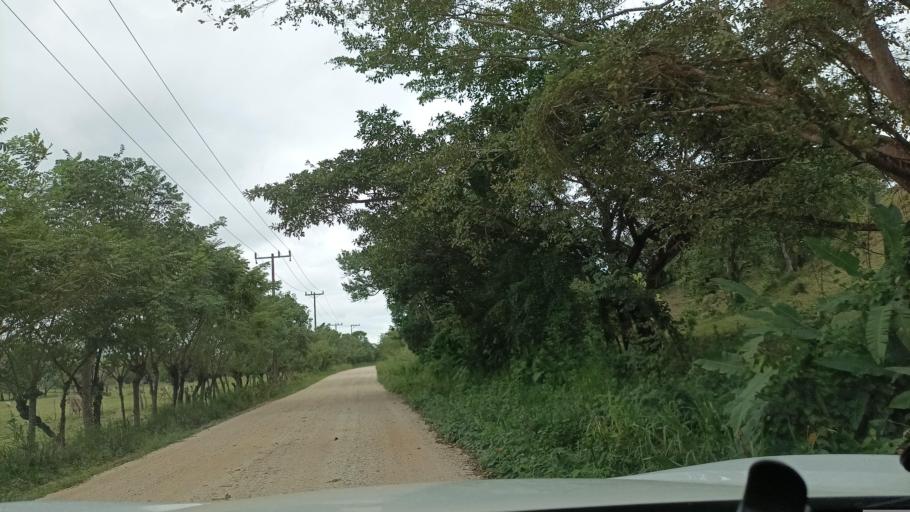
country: MX
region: Veracruz
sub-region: Moloacan
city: Cuichapa
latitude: 17.8448
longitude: -94.3604
